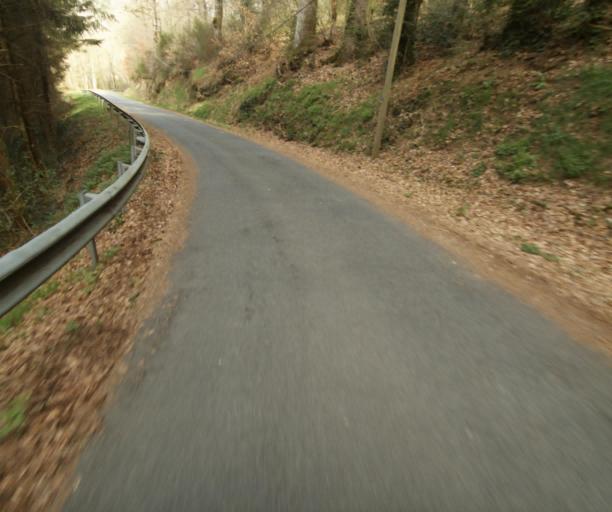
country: FR
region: Limousin
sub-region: Departement de la Correze
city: Correze
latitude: 45.4240
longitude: 1.8026
